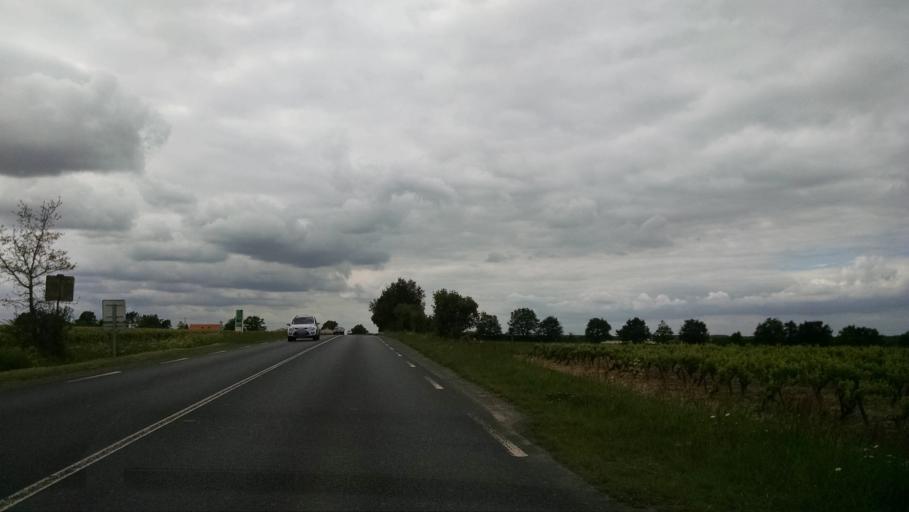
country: FR
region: Pays de la Loire
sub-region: Departement de la Loire-Atlantique
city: Aigrefeuille-sur-Maine
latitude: 47.0833
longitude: -1.4172
